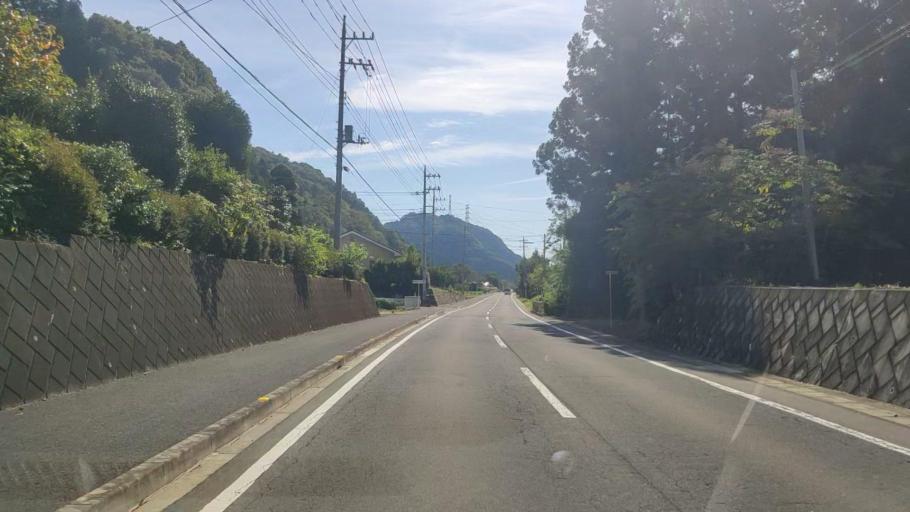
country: JP
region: Gunma
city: Nakanojomachi
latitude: 36.6132
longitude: 138.7831
